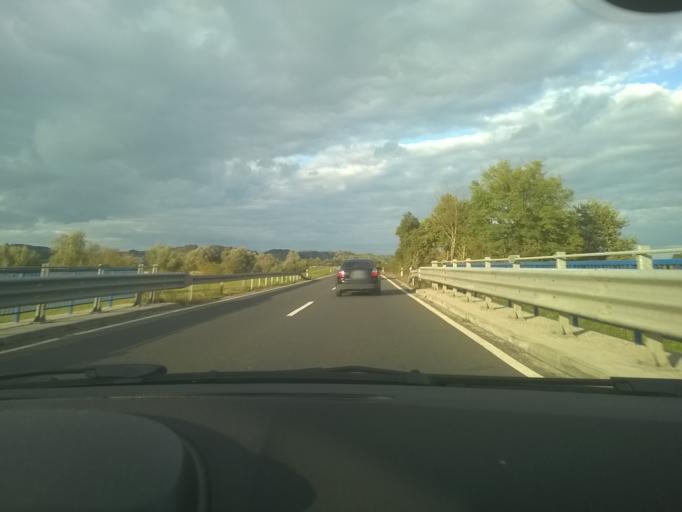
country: HR
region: Zagrebacka
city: Jakovlje
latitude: 45.9424
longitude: 15.8234
